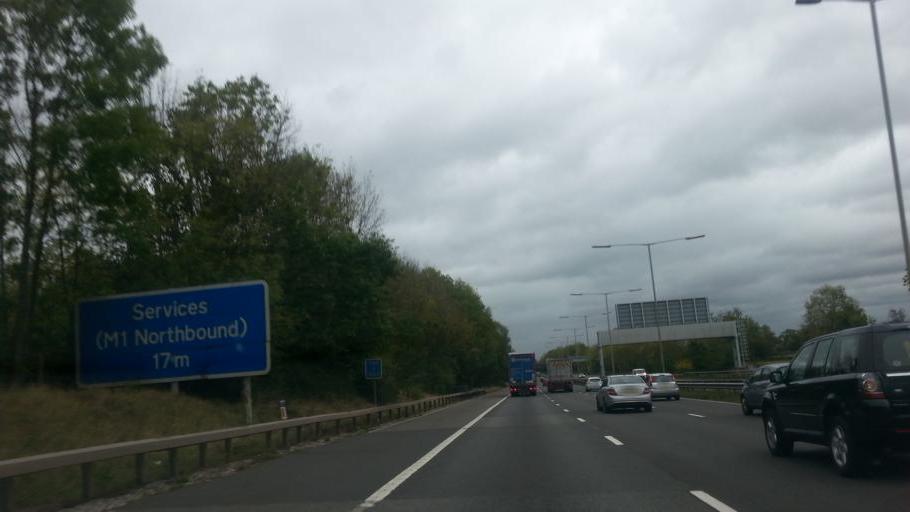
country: GB
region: England
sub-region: Warwickshire
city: Bedworth
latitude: 52.4526
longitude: -1.4214
